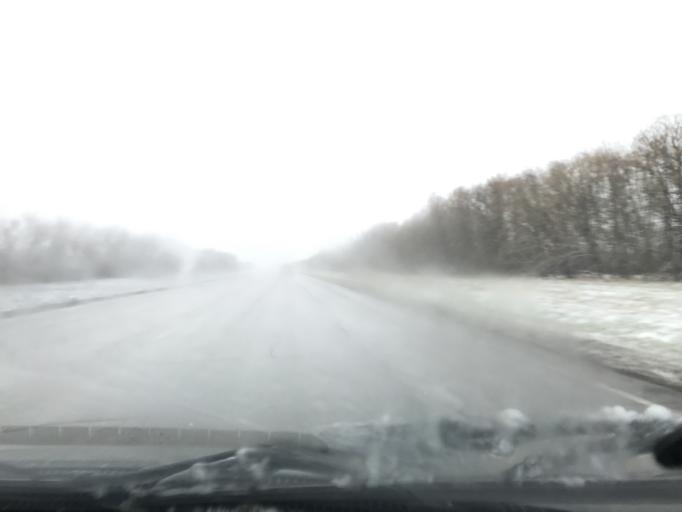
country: RU
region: Rostov
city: Yegorlykskaya
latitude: 46.6318
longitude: 40.5871
